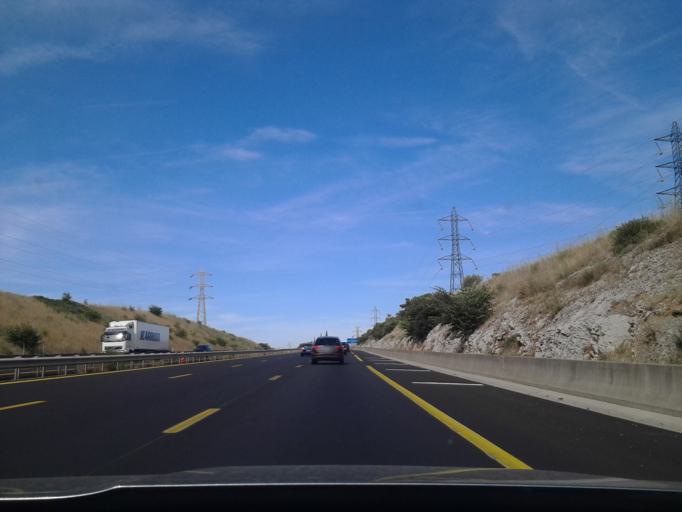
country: FR
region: Languedoc-Roussillon
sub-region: Departement de l'Herault
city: Saint-Jean-de-Vedas
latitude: 43.5510
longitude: 3.8099
